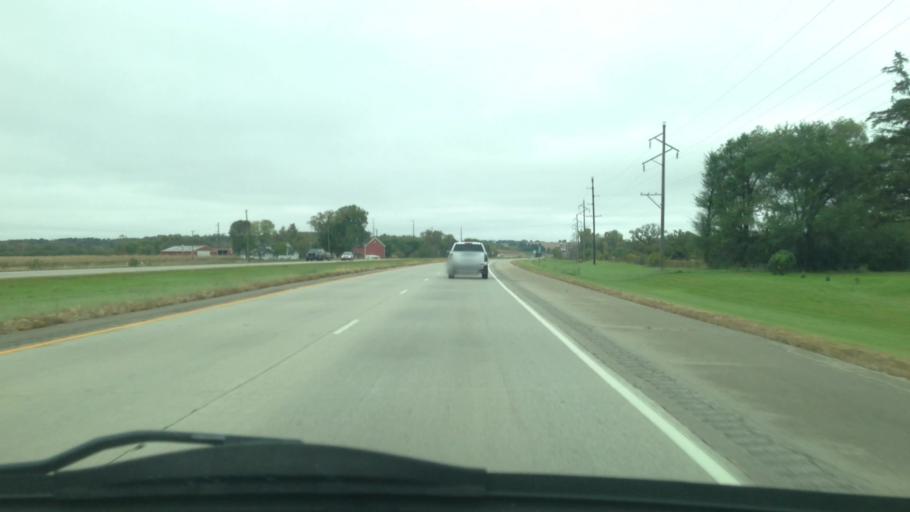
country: US
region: Minnesota
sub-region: Goodhue County
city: Zumbrota
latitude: 44.3133
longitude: -92.6980
